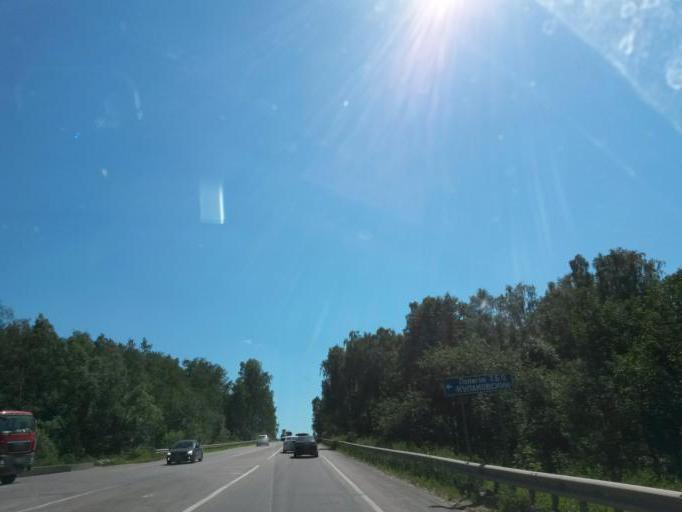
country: RU
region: Moskovskaya
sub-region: Chekhovskiy Rayon
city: Chekhov
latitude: 55.1087
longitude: 37.4465
